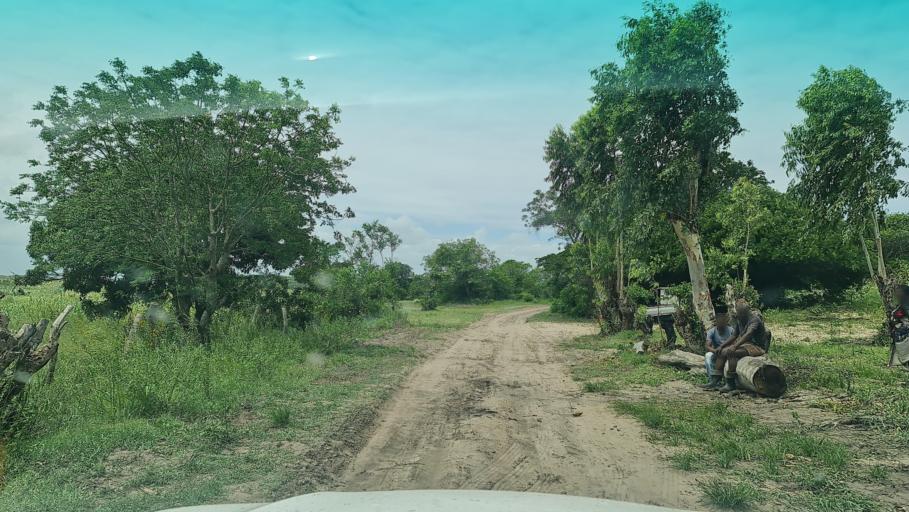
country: MZ
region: Maputo
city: Manhica
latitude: -25.5188
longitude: 32.8658
